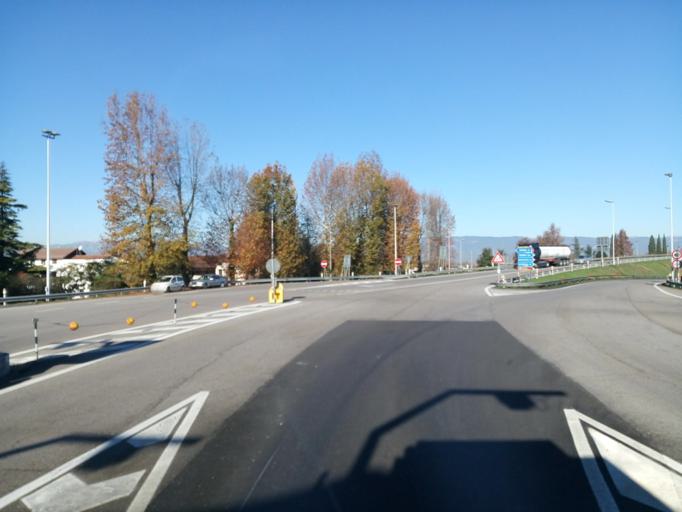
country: IT
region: Veneto
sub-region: Provincia di Vicenza
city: Lisiera
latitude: 45.5790
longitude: 11.5990
